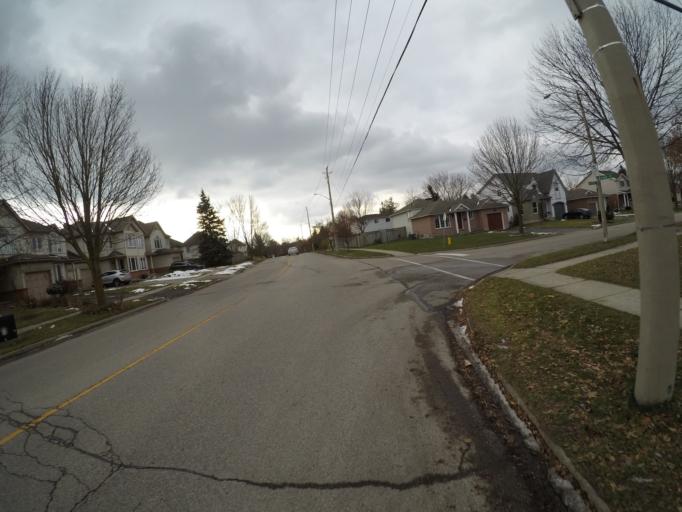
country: CA
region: Ontario
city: Waterloo
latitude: 43.4865
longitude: -80.4863
